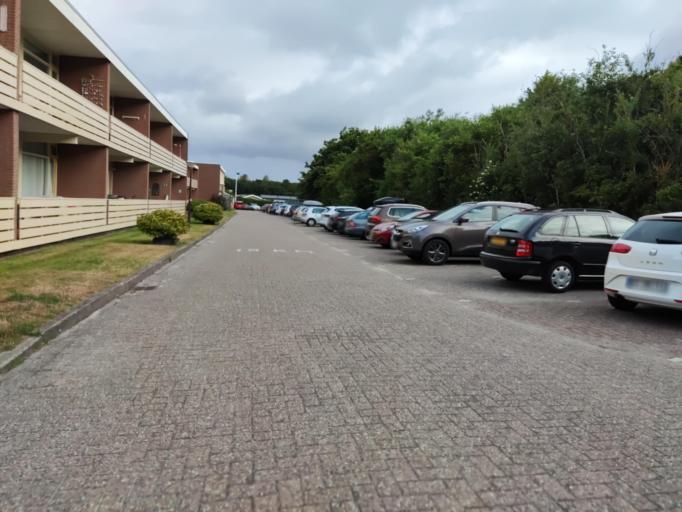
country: NL
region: North Holland
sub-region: Gemeente Texel
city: Den Burg
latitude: 53.0906
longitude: 4.7668
